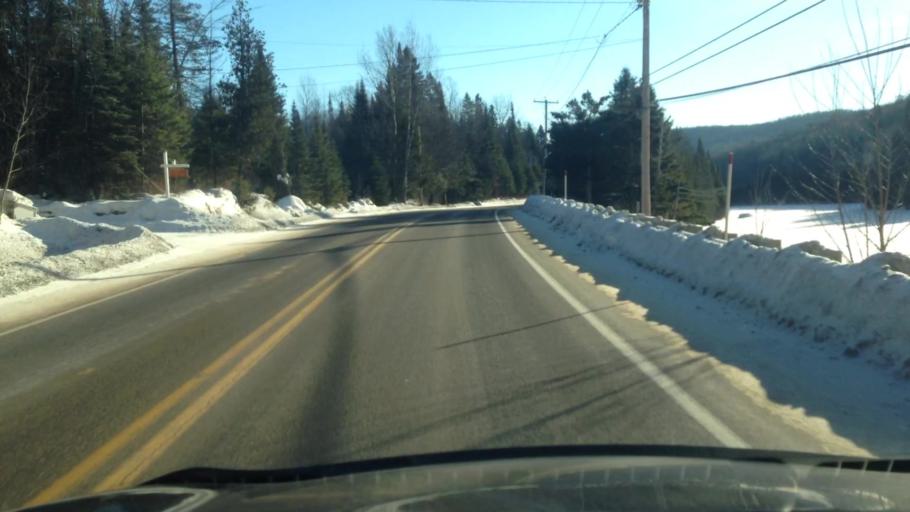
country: CA
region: Quebec
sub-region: Laurentides
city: Sainte-Agathe-des-Monts
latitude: 45.9077
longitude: -74.3276
